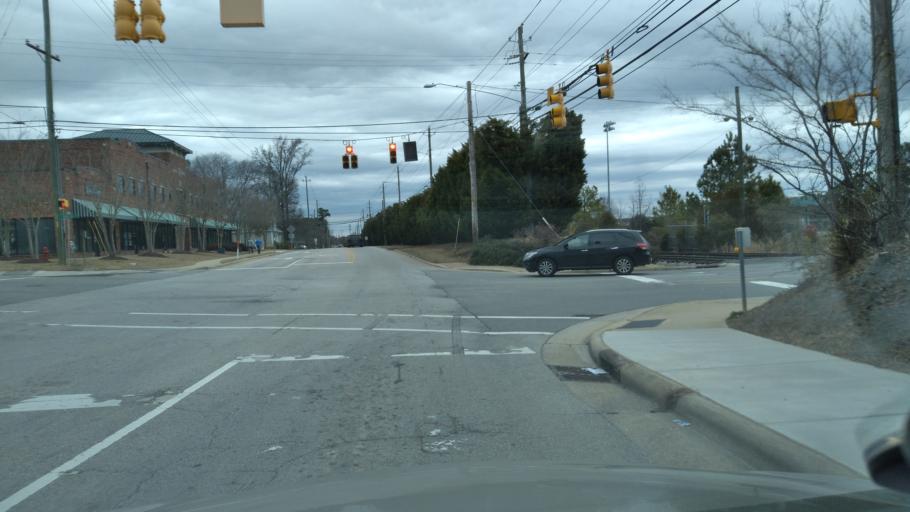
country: US
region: North Carolina
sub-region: Wake County
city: Apex
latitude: 35.7355
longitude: -78.8490
